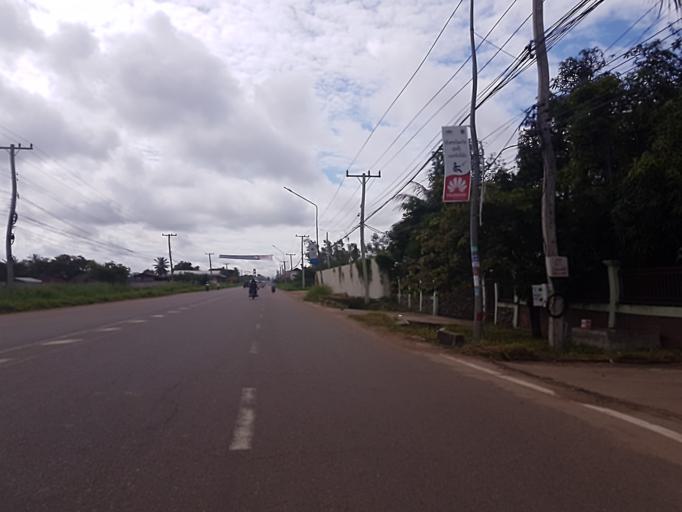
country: TH
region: Nong Khai
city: Tha Bo
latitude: 17.8868
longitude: 102.6473
